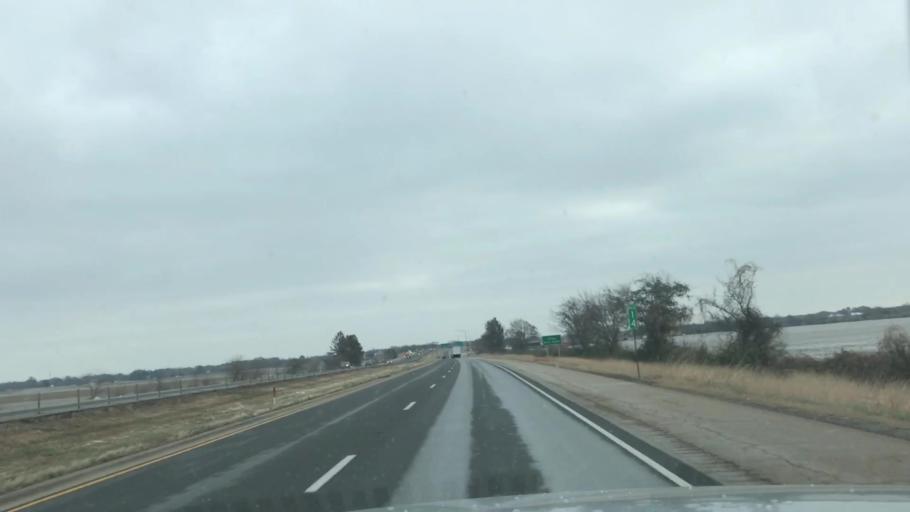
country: US
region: Illinois
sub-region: Madison County
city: Troy
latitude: 38.7517
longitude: -89.9198
